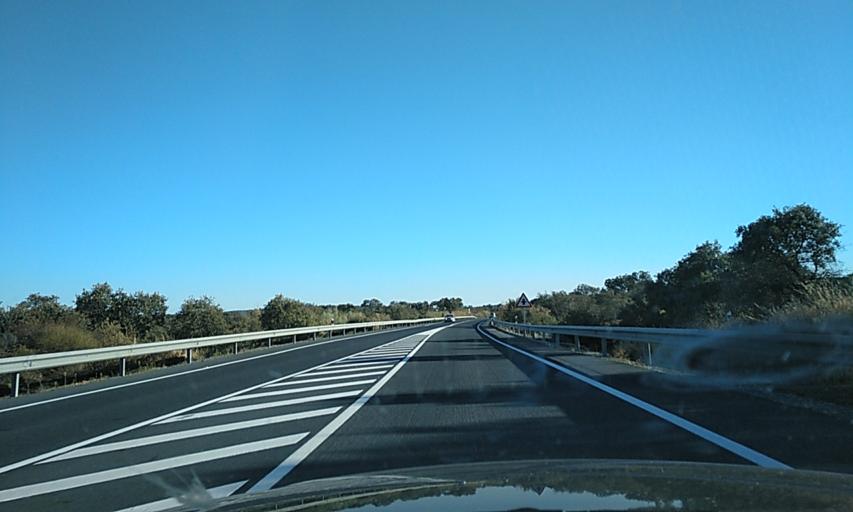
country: ES
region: Andalusia
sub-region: Provincia de Huelva
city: San Bartolome de la Torre
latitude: 37.4630
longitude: -7.1242
